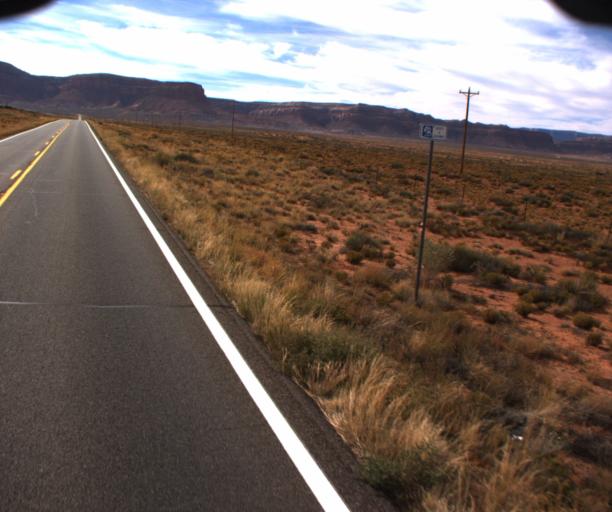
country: US
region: Arizona
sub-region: Navajo County
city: Kayenta
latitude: 36.8864
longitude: -110.2496
